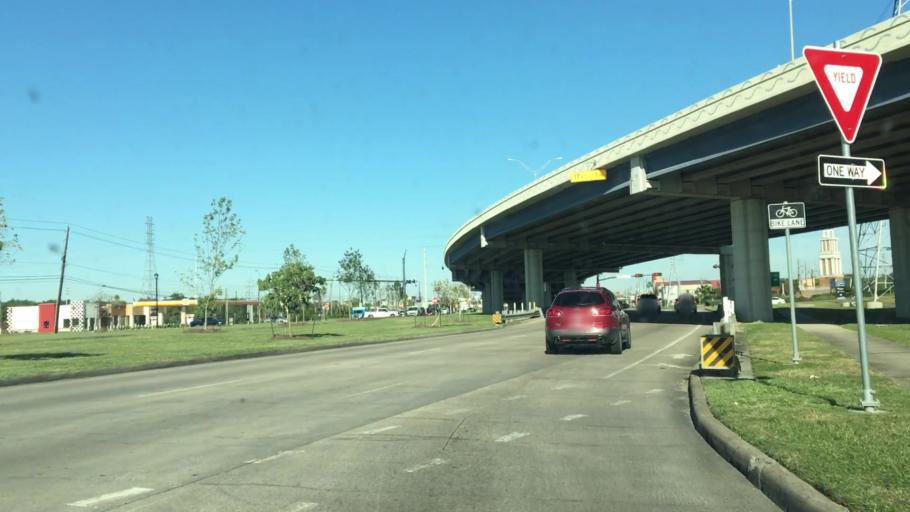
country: US
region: Texas
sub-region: Harris County
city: Webster
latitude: 29.5415
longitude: -95.1123
